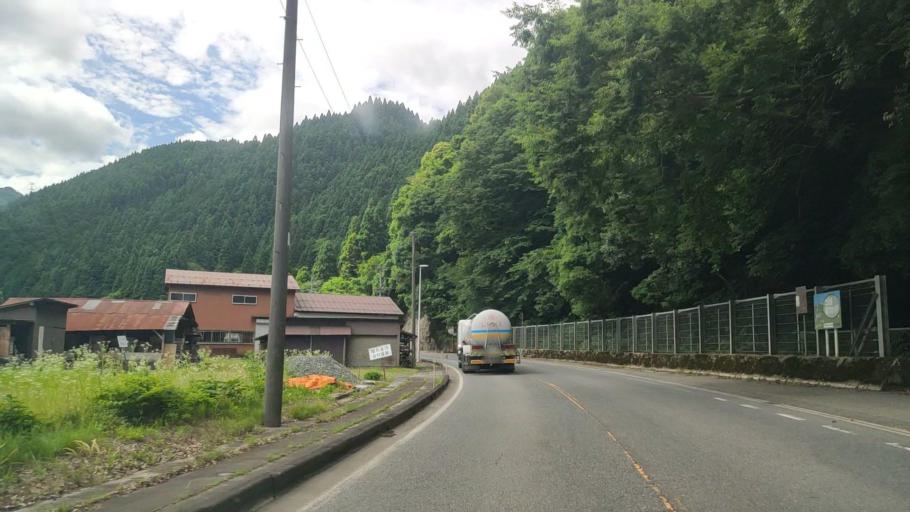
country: JP
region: Tottori
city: Yonago
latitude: 35.2343
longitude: 133.4393
